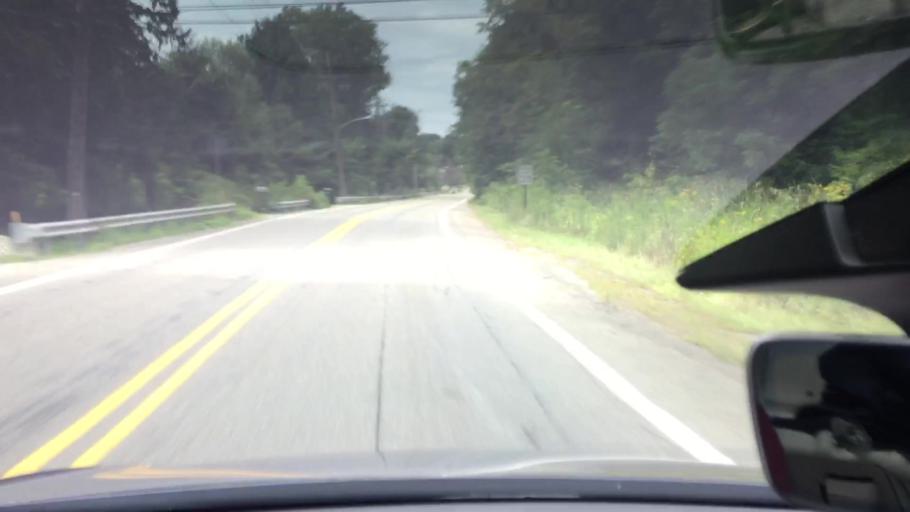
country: US
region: Pennsylvania
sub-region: Allegheny County
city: Monroeville
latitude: 40.4481
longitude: -79.8073
